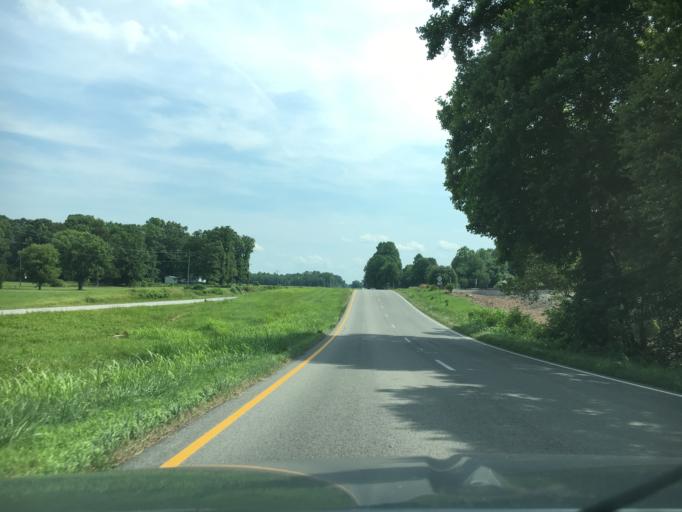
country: US
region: Virginia
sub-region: Nottoway County
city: Crewe
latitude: 37.2550
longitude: -78.1399
